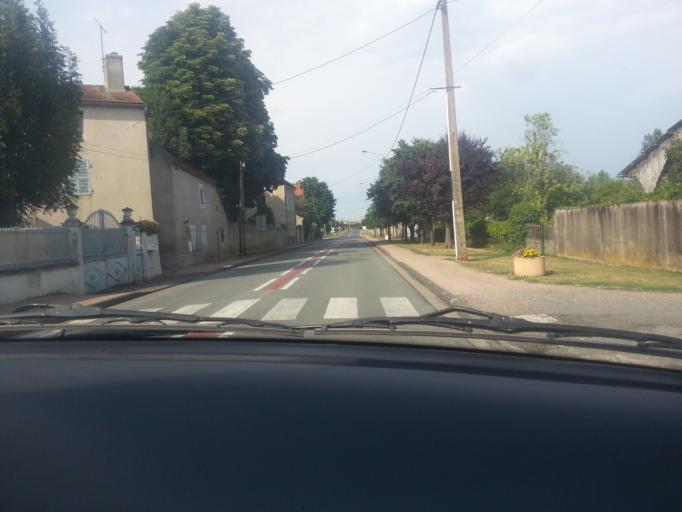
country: FR
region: Auvergne
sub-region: Departement du Puy-de-Dome
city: Aigueperse
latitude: 46.0430
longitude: 3.2561
